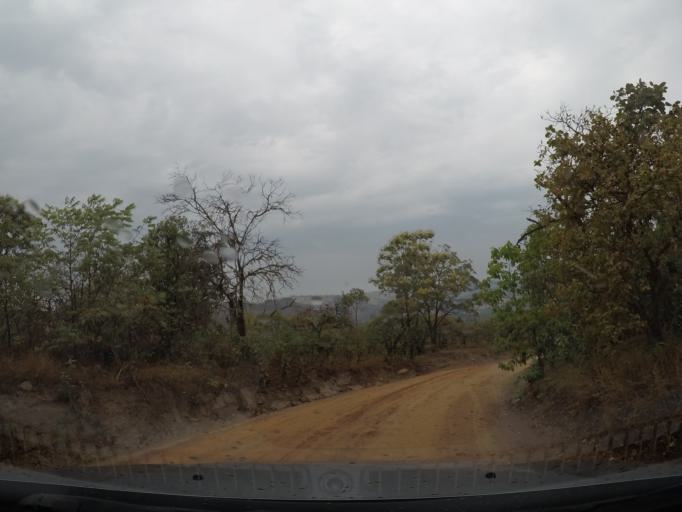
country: BR
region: Goias
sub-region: Pirenopolis
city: Pirenopolis
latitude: -15.8382
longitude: -48.9120
